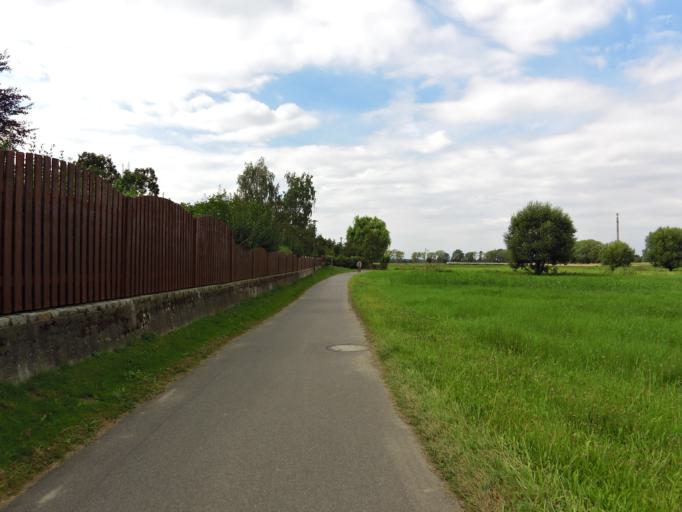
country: DE
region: Saxony
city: Coswig
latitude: 51.0983
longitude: 13.5944
